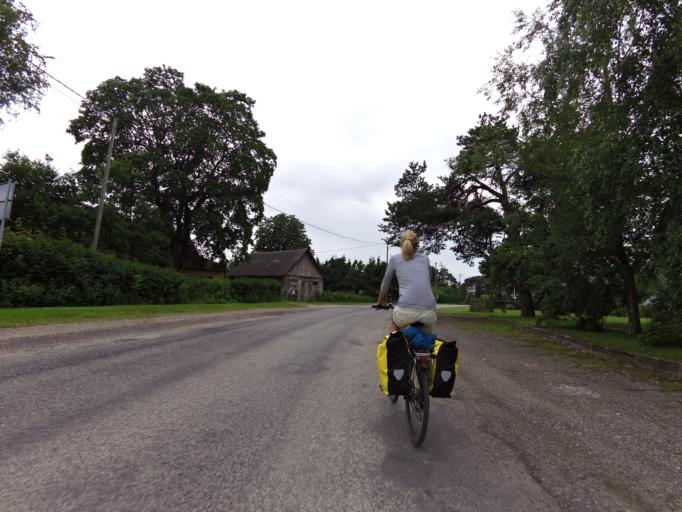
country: EE
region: Harju
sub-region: Nissi vald
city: Turba
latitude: 58.9973
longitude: 24.0582
